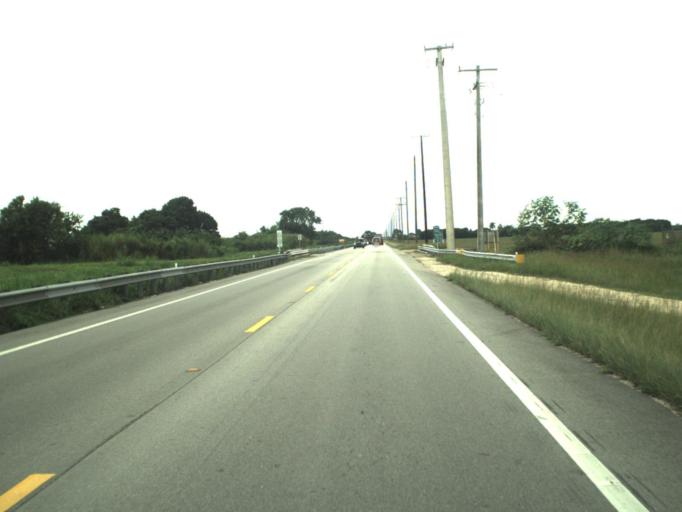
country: US
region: Florida
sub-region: Miami-Dade County
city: The Hammocks
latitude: 25.6619
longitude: -80.4809
